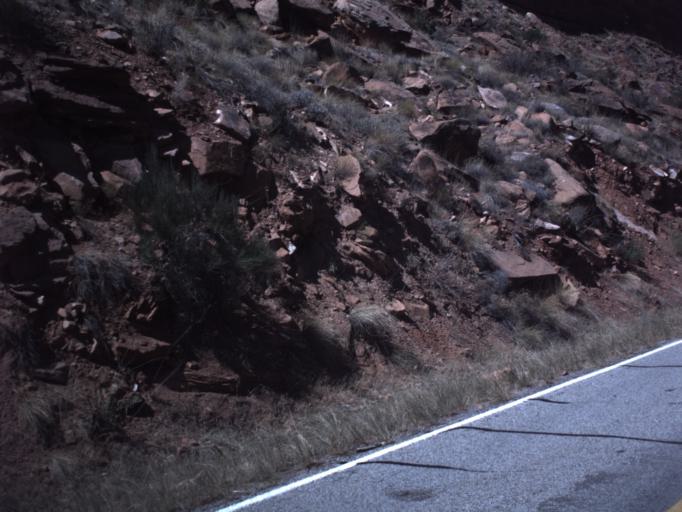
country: US
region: Utah
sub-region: Grand County
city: Moab
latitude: 38.7991
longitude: -109.3327
